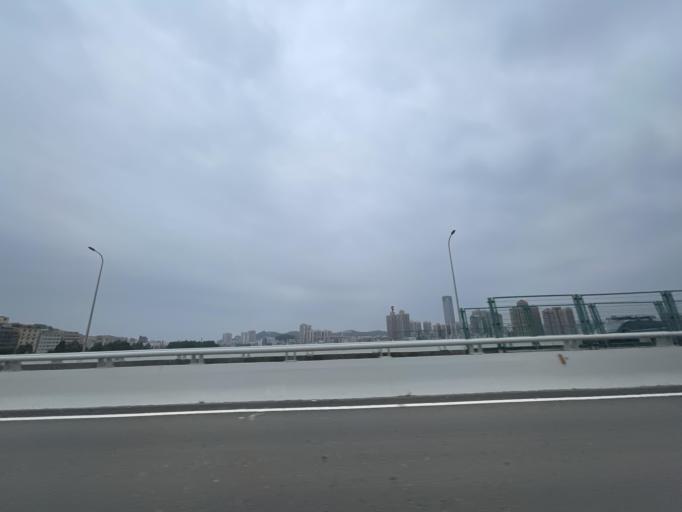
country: CN
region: Guangdong
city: Humen
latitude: 22.8068
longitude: 113.6641
